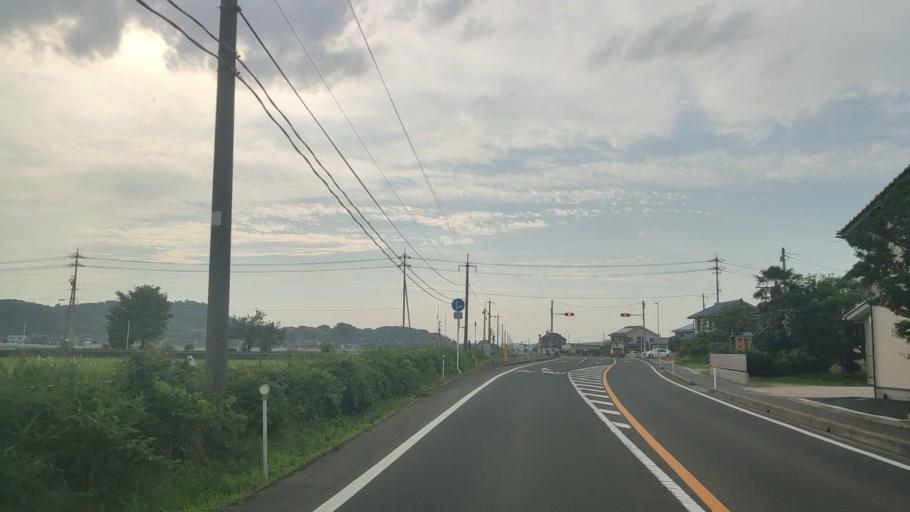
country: JP
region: Tottori
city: Kurayoshi
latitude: 35.4757
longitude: 133.8212
